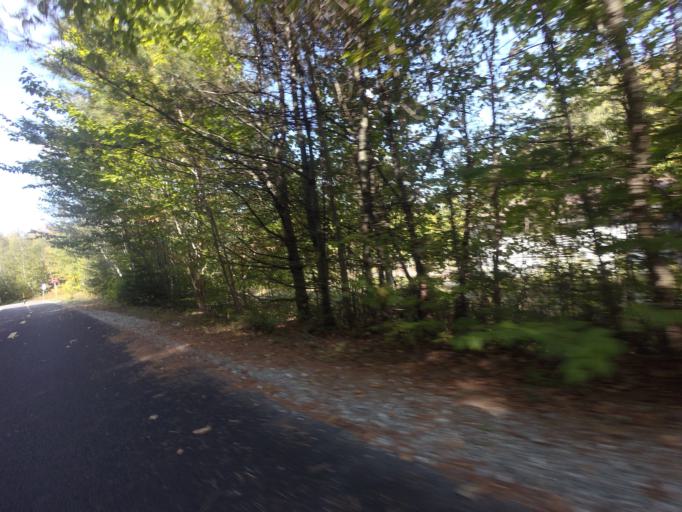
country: CA
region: Quebec
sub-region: Laurentides
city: Mont-Tremblant
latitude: 46.1336
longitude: -74.4784
